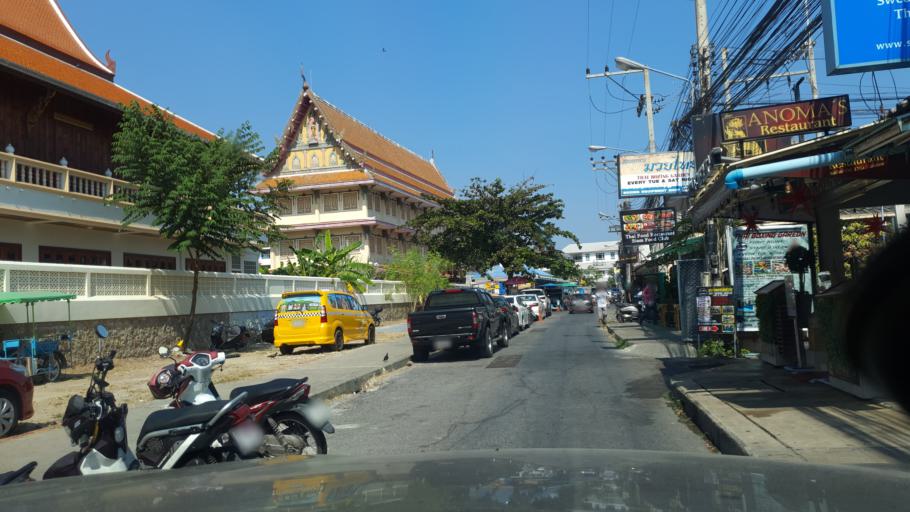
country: TH
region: Prachuap Khiri Khan
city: Hua Hin
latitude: 12.5697
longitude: 99.9587
